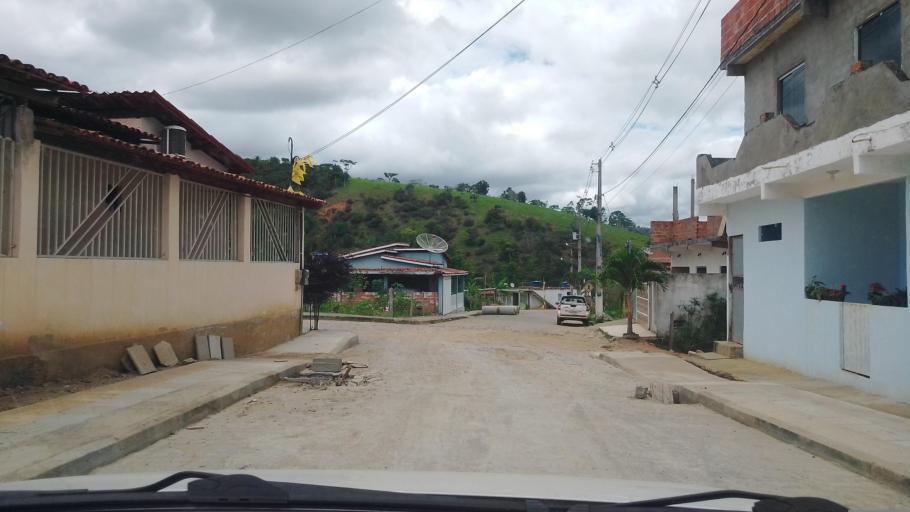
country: BR
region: Bahia
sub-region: Mutuipe
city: Mutuipe
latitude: -13.2571
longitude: -39.5655
